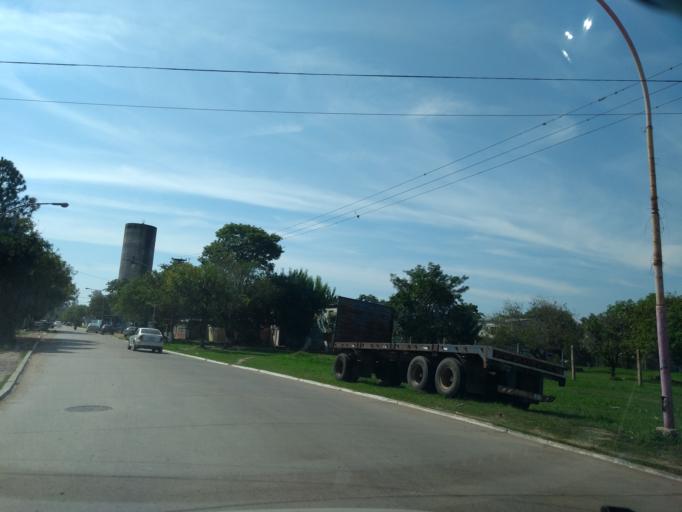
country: AR
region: Chaco
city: Barranqueras
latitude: -27.4651
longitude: -58.9501
